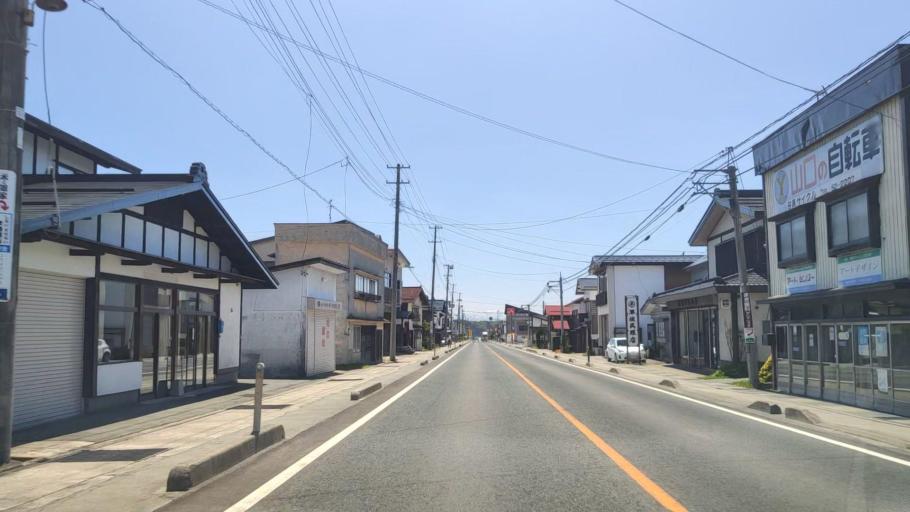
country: JP
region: Yamagata
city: Shinjo
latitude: 38.8815
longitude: 140.3365
